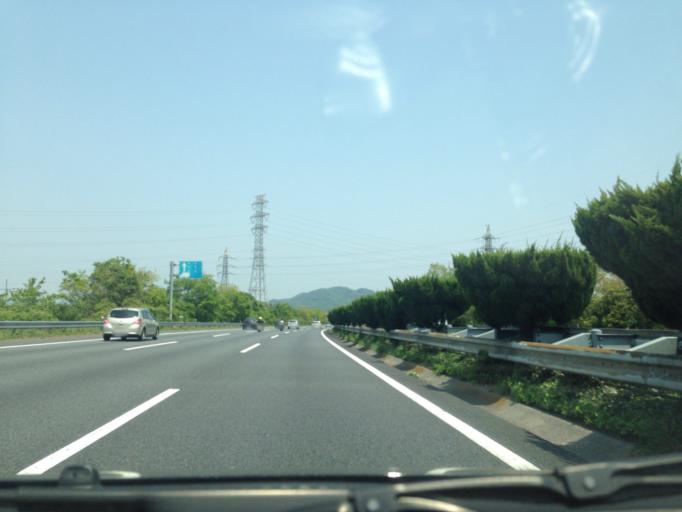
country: JP
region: Tochigi
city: Sano
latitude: 36.2717
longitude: 139.6024
